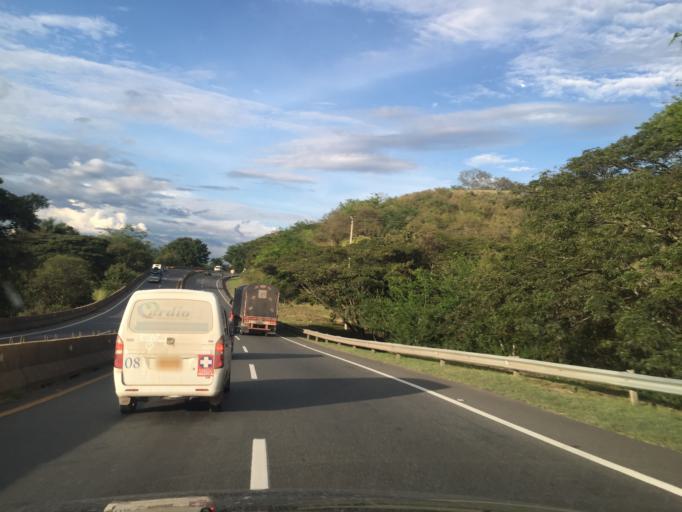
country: CO
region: Valle del Cauca
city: Bugalagrande
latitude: 4.2072
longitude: -76.1532
